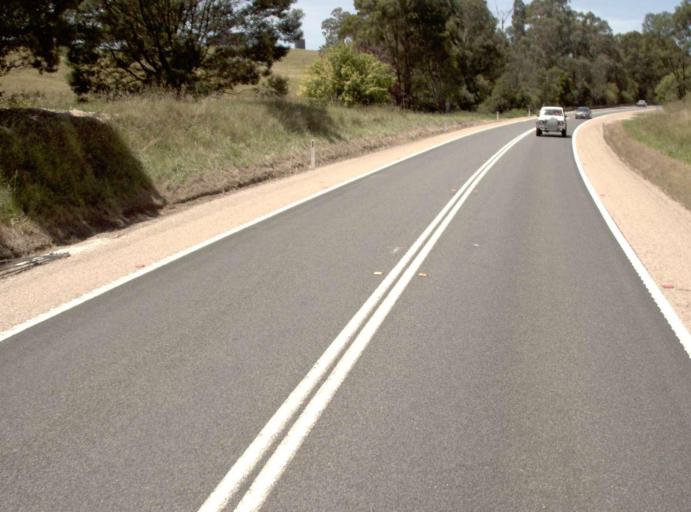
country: AU
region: Victoria
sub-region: East Gippsland
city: Bairnsdale
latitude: -37.7508
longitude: 147.7295
